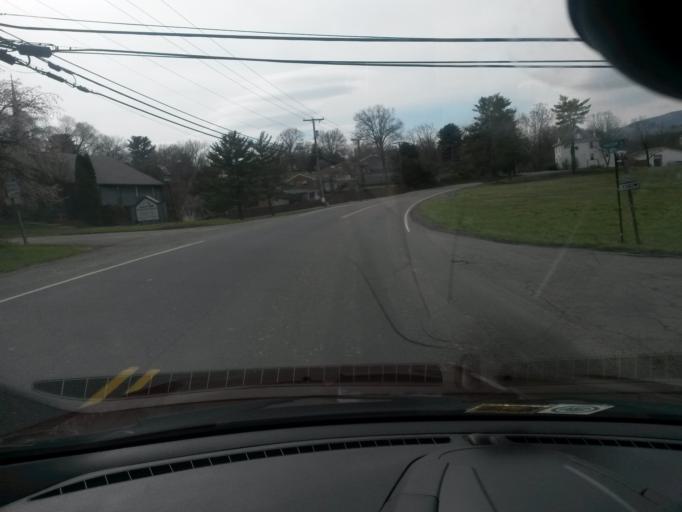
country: US
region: Virginia
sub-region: Roanoke County
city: Cave Spring
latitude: 37.2427
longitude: -80.0066
